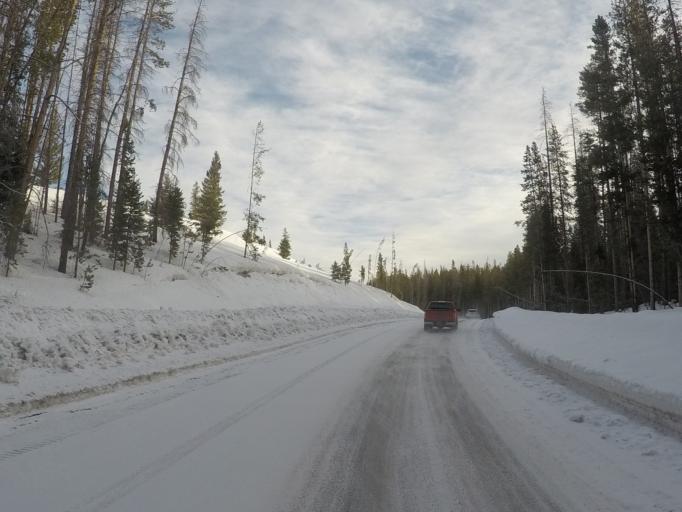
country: US
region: Montana
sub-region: Granite County
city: Philipsburg
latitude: 46.2202
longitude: -113.2556
